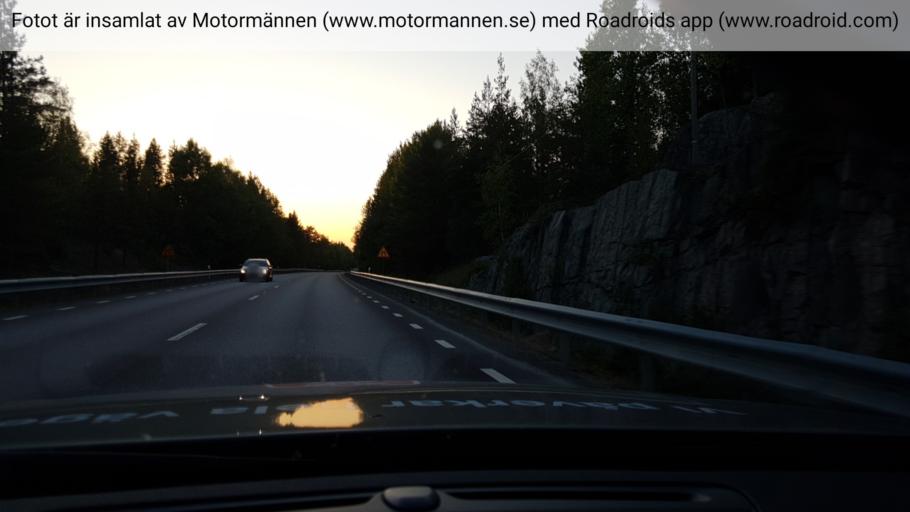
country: SE
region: Uppsala
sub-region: Osthammars Kommun
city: Bjorklinge
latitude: 59.9827
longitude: 17.3339
